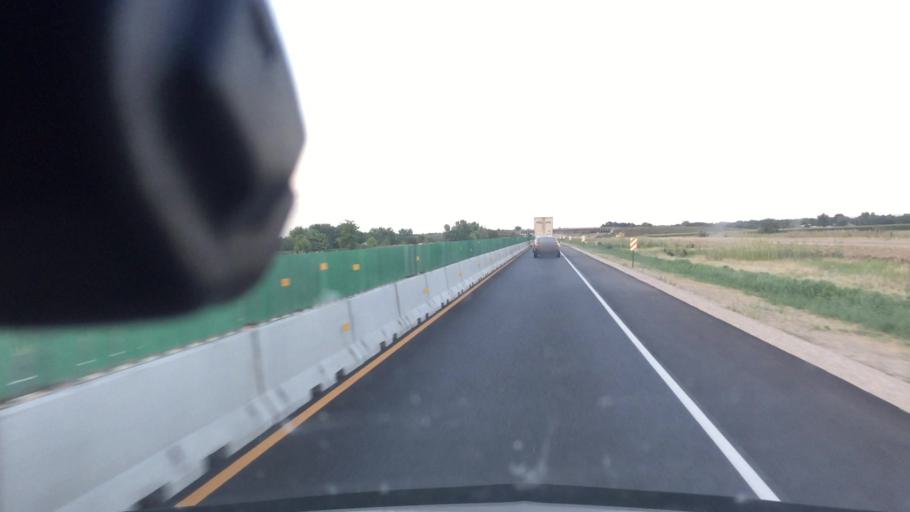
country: US
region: Illinois
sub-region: Livingston County
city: Pontiac
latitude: 40.9390
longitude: -88.5996
